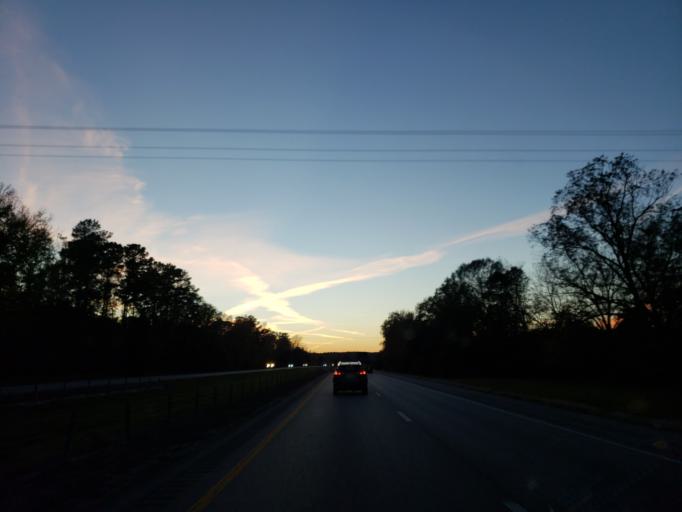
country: US
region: Mississippi
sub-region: Lauderdale County
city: Marion
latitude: 32.4117
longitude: -88.4695
